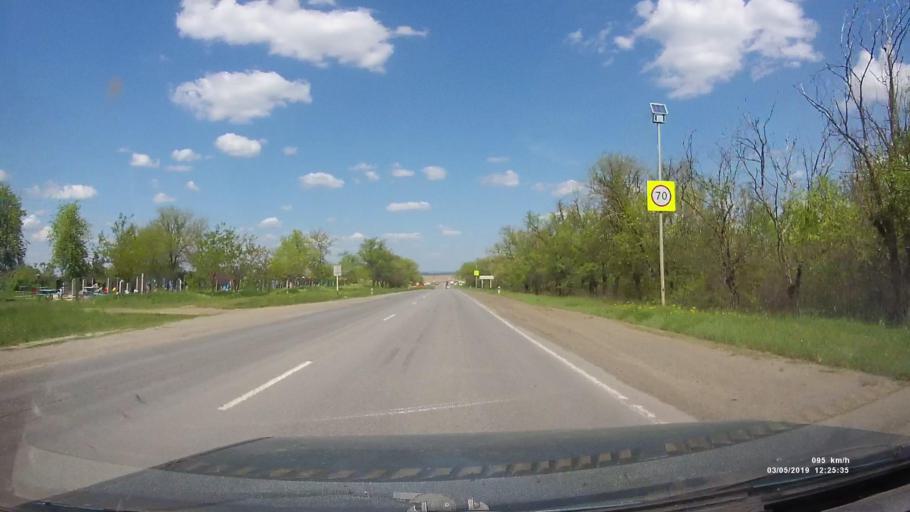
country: RU
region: Rostov
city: Semikarakorsk
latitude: 47.4350
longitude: 40.7117
